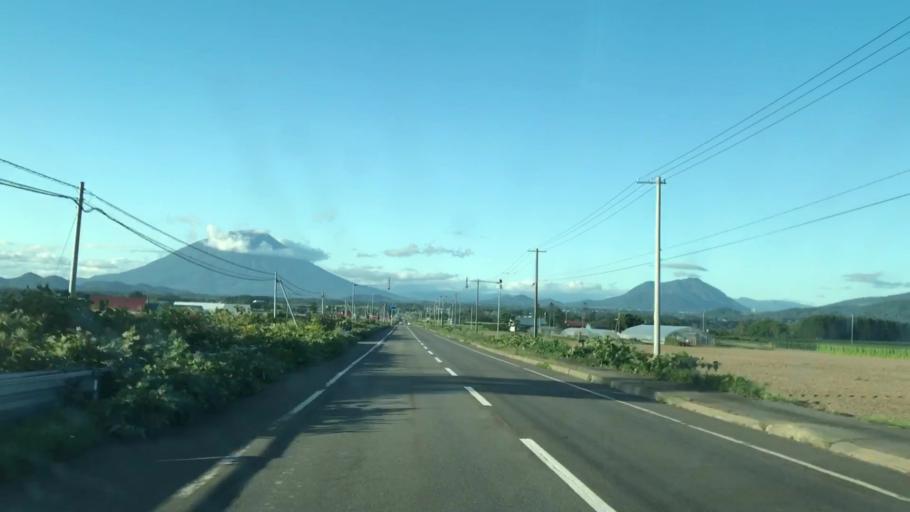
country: JP
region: Hokkaido
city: Date
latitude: 42.6312
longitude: 140.8003
